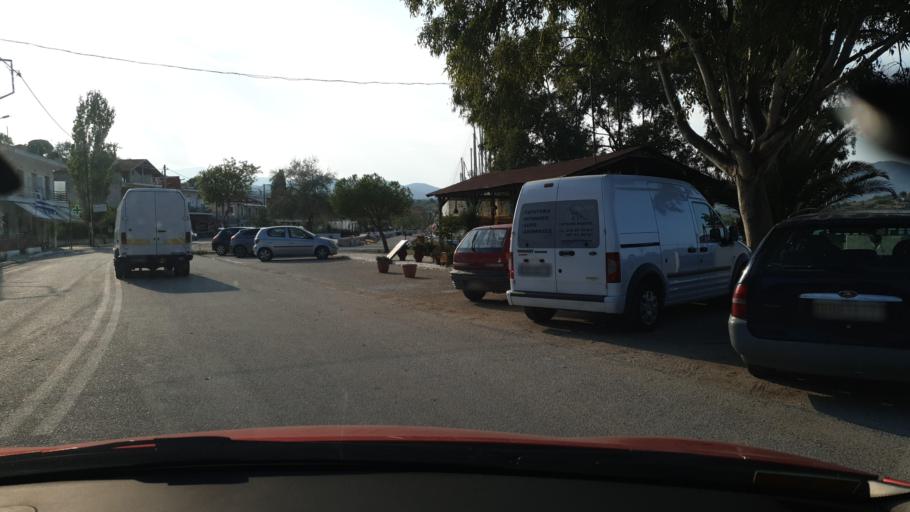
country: GR
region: Thessaly
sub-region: Nomos Magnisias
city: Pteleos
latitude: 39.0054
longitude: 22.9639
